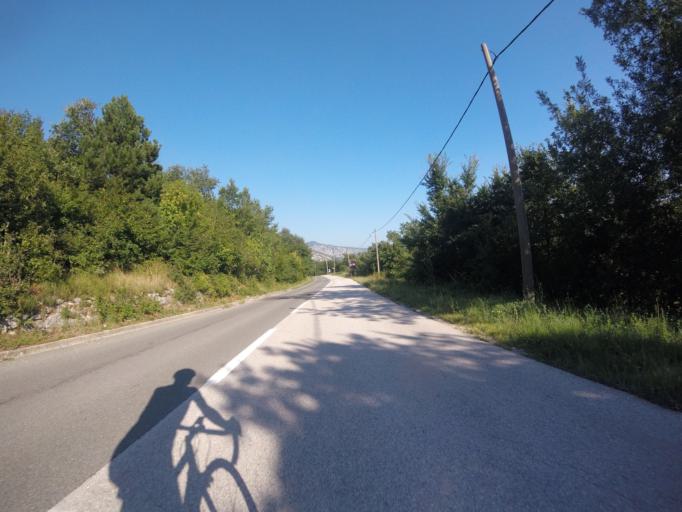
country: HR
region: Primorsko-Goranska
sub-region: Grad Crikvenica
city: Jadranovo
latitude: 45.2426
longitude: 14.6434
